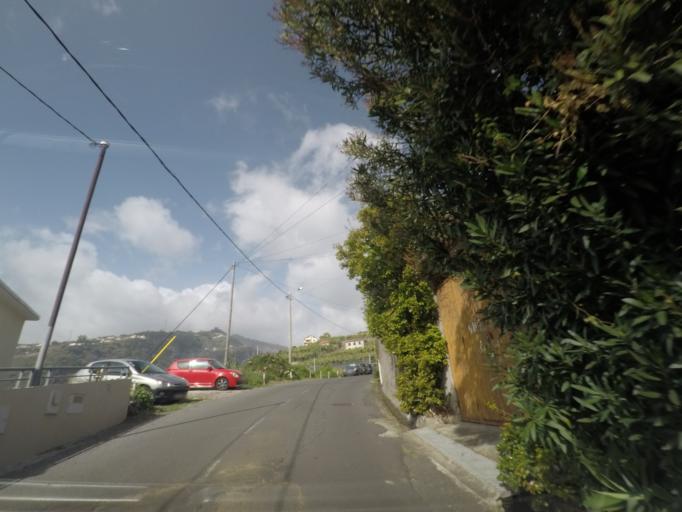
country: PT
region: Madeira
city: Ribeira Brava
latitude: 32.6719
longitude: -17.0594
